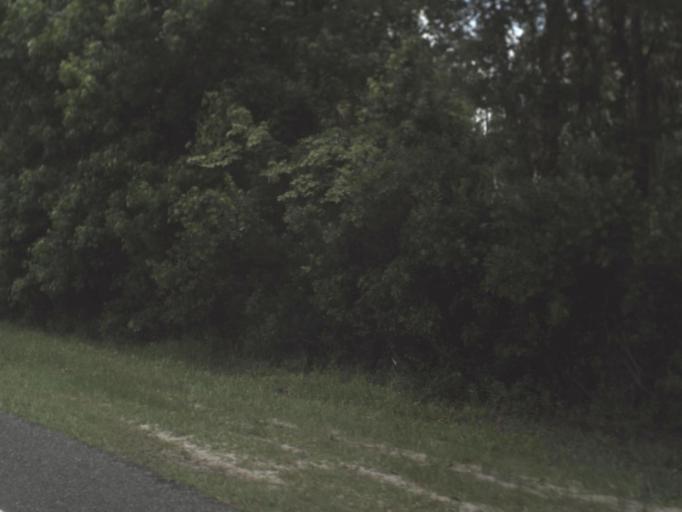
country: US
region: Florida
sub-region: Nassau County
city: Hilliard
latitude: 30.6531
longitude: -81.8761
